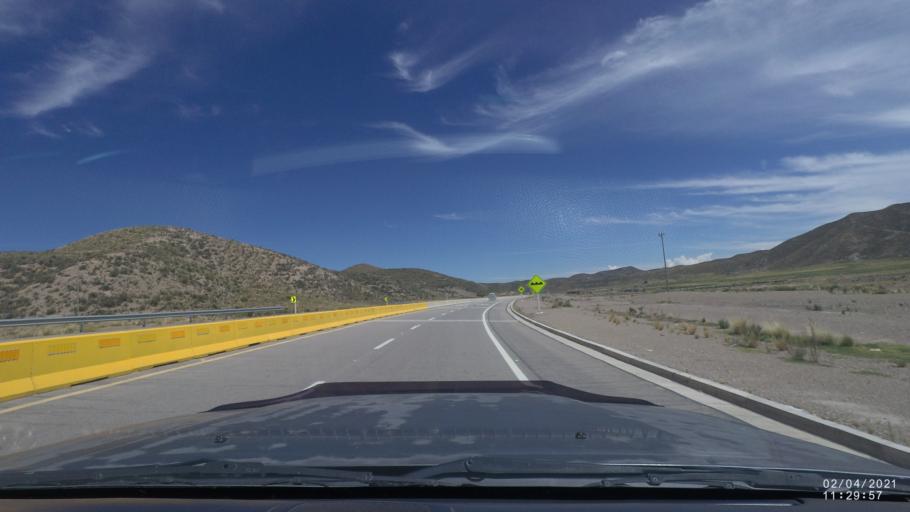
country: BO
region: La Paz
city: Colquiri
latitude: -17.6627
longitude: -66.9997
